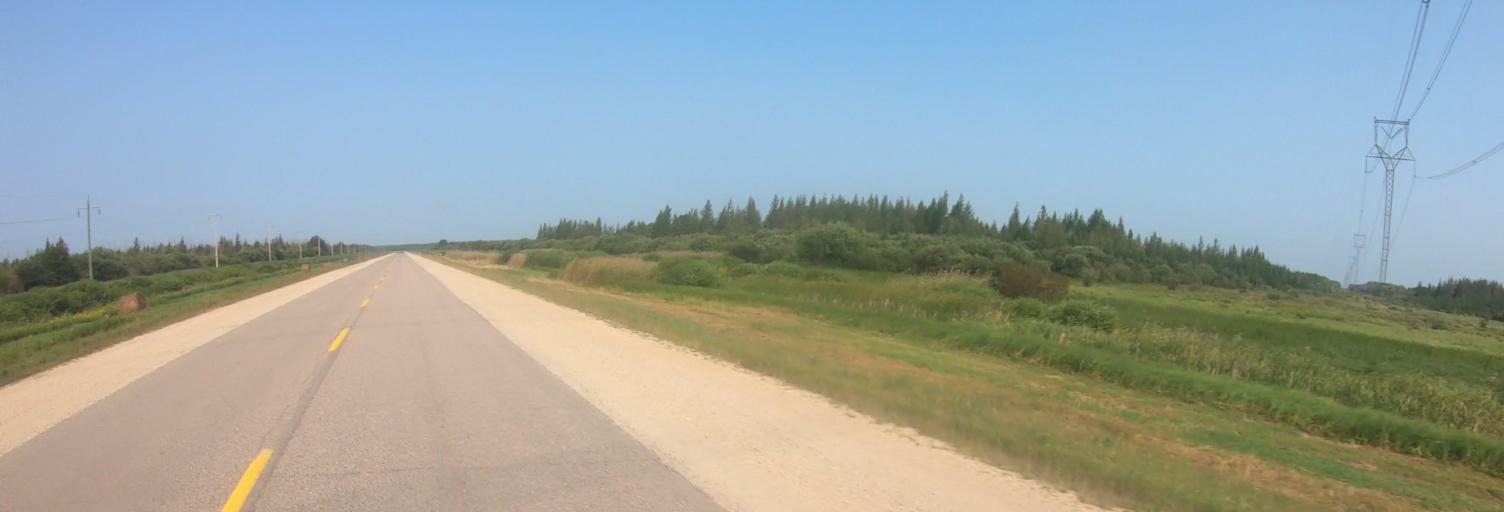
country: US
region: Minnesota
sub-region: Roseau County
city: Warroad
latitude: 49.0169
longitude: -95.5402
